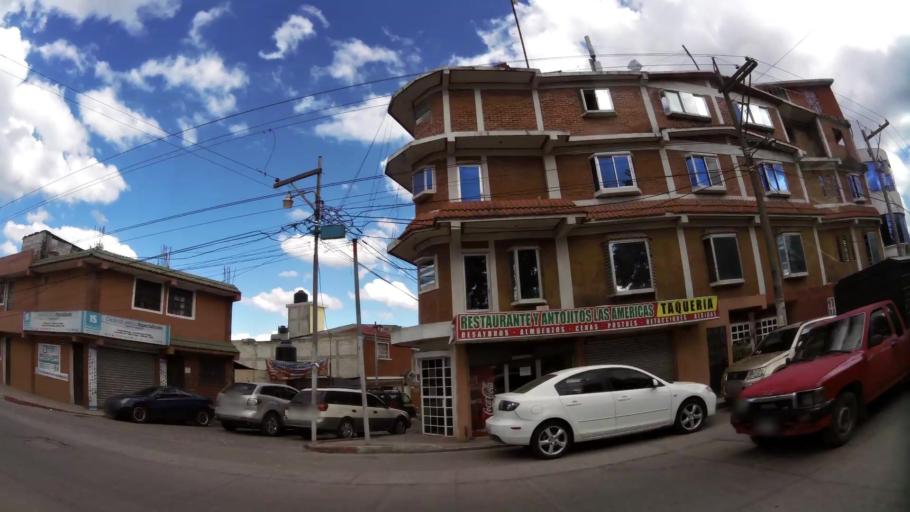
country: GT
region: Quetzaltenango
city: Quetzaltenango
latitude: 14.8434
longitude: -91.5363
